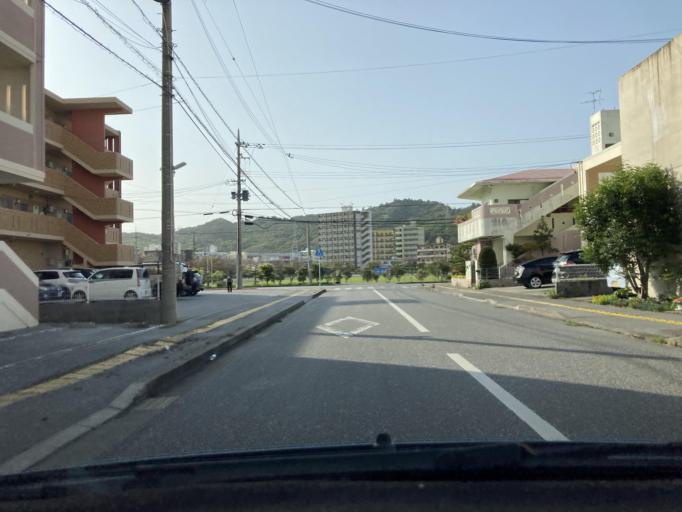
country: JP
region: Okinawa
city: Ginowan
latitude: 26.2069
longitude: 127.7604
